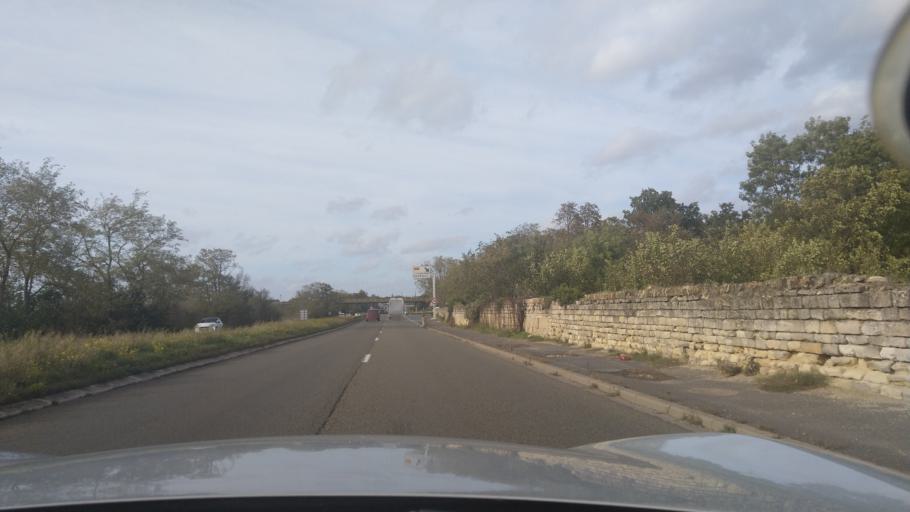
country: FR
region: Ile-de-France
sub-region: Departement des Yvelines
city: Conflans-Sainte-Honorine
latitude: 48.9779
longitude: 2.0881
